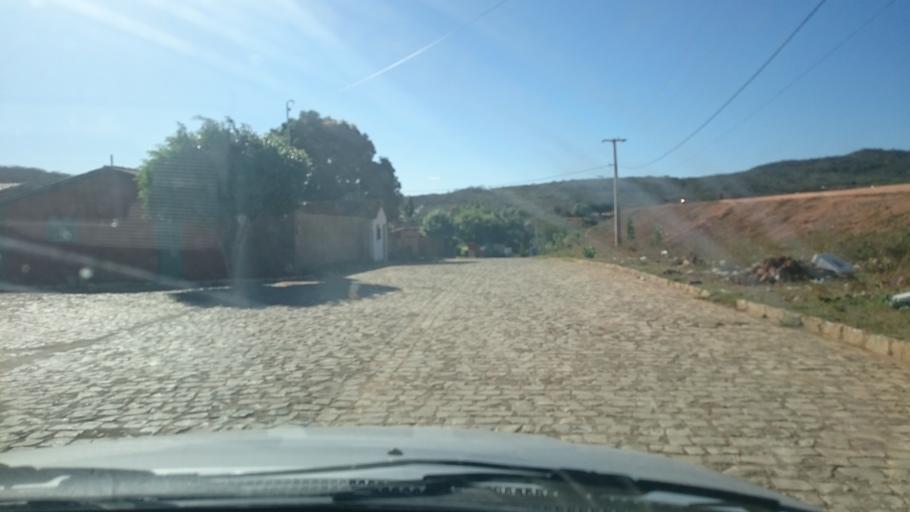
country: BR
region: Paraiba
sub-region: Catole Do Rocha
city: Sao Bento
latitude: -6.1637
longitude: -37.7620
